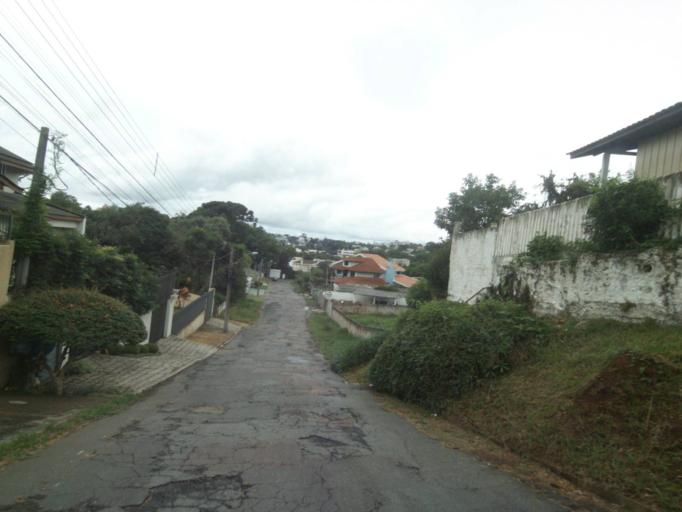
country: BR
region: Parana
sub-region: Curitiba
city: Curitiba
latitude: -25.4490
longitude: -49.3183
